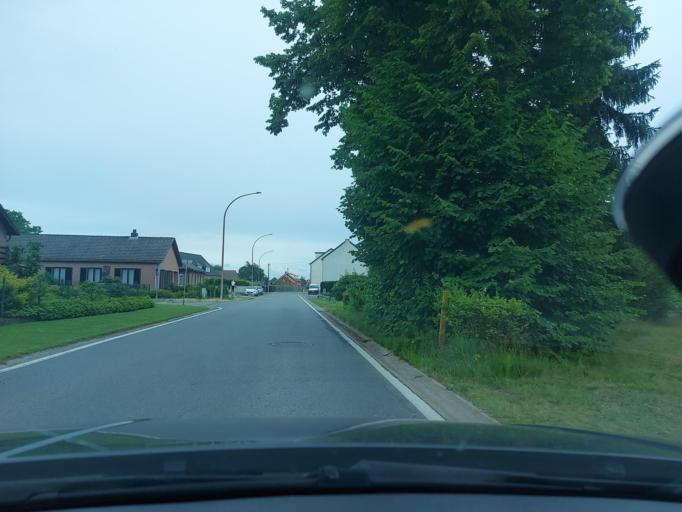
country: BE
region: Flanders
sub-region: Provincie Antwerpen
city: Balen
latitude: 51.1853
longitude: 5.2282
